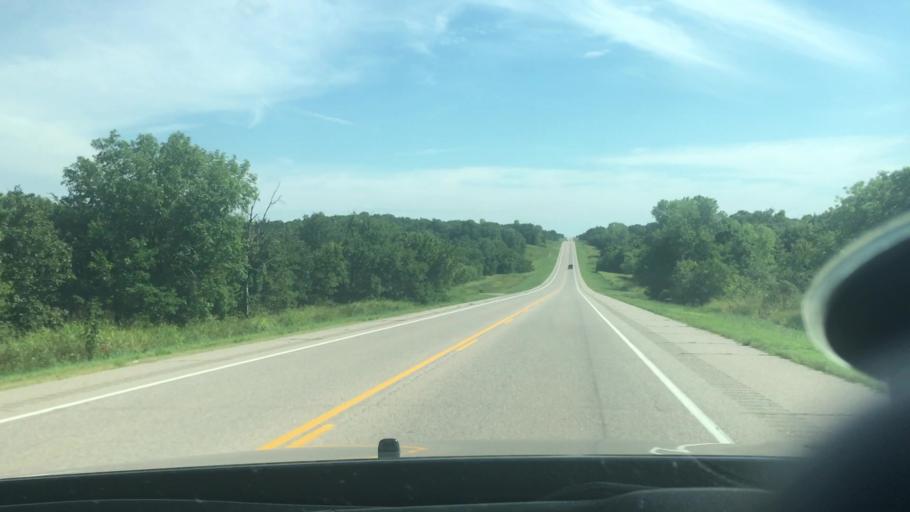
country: US
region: Oklahoma
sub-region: Seminole County
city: Maud
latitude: 35.1135
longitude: -96.6789
